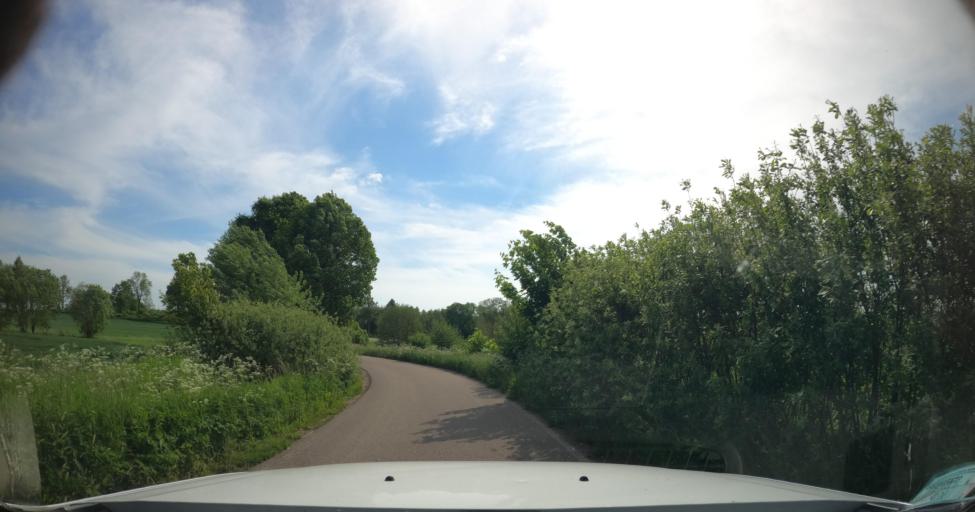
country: PL
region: Warmian-Masurian Voivodeship
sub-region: Powiat ostrodzki
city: Milakowo
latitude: 54.0143
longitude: 20.1528
